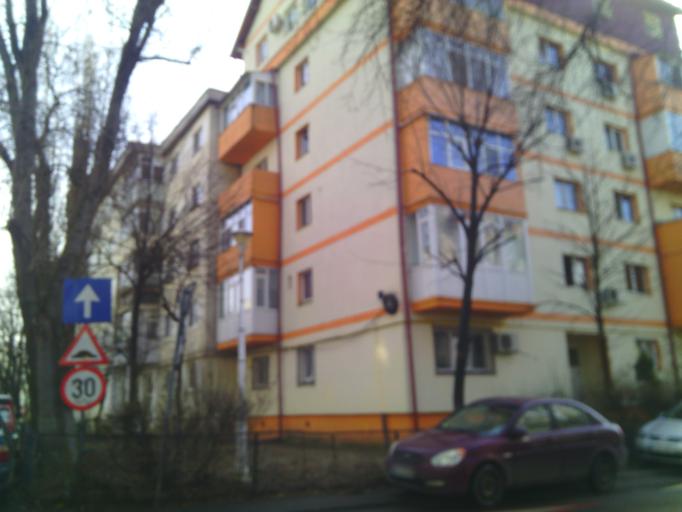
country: RO
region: Bucuresti
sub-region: Municipiul Bucuresti
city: Bucuresti
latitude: 44.3840
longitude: 26.0944
